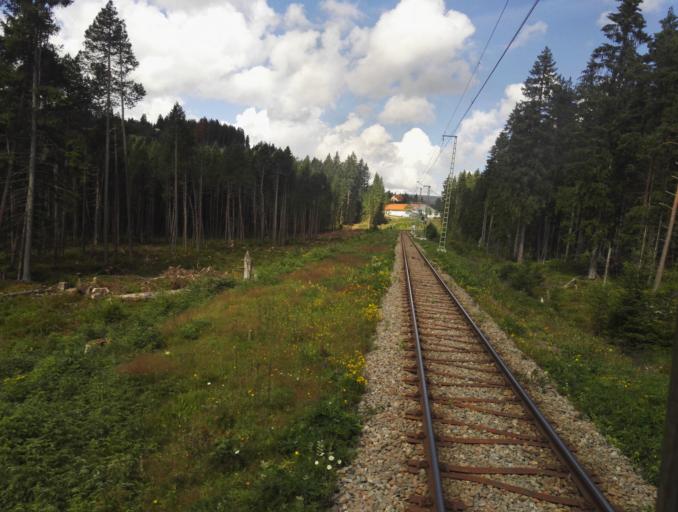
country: DE
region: Baden-Wuerttemberg
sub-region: Freiburg Region
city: Hinterzarten
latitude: 47.8669
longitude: 8.1016
